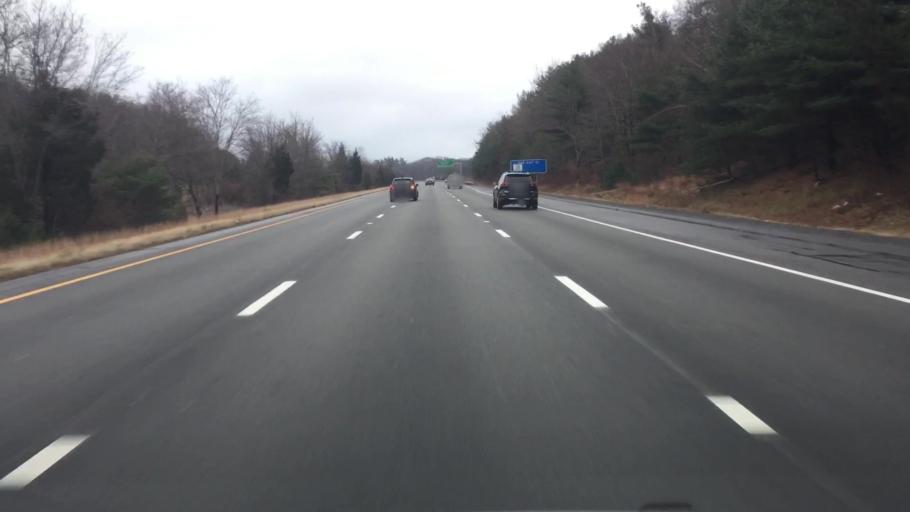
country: US
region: Massachusetts
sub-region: Norfolk County
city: Franklin
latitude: 42.0687
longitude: -71.4071
